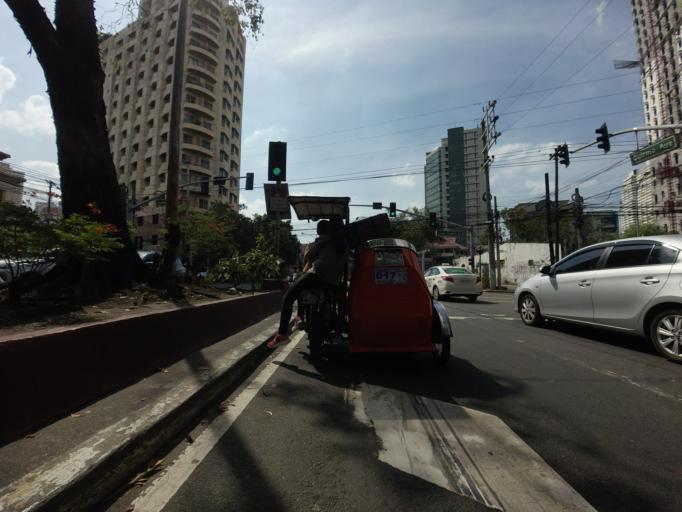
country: PH
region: Metro Manila
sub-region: City of Manila
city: Port Area
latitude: 14.5713
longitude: 120.9923
